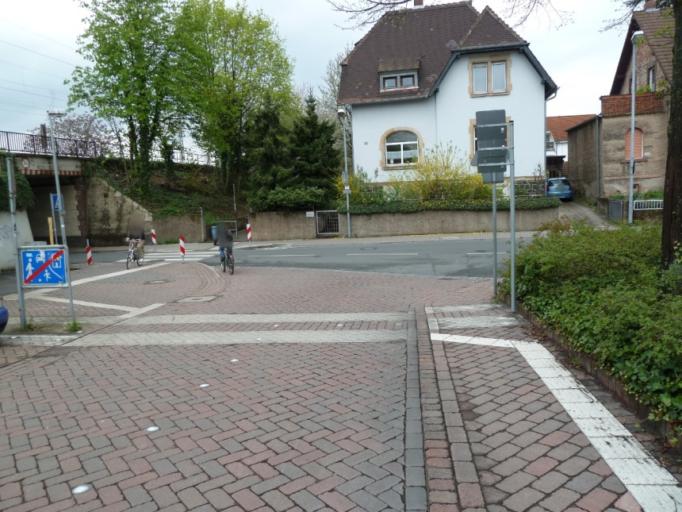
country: DE
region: Hesse
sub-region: Regierungsbezirk Darmstadt
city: Bensheim
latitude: 49.6823
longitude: 8.6170
